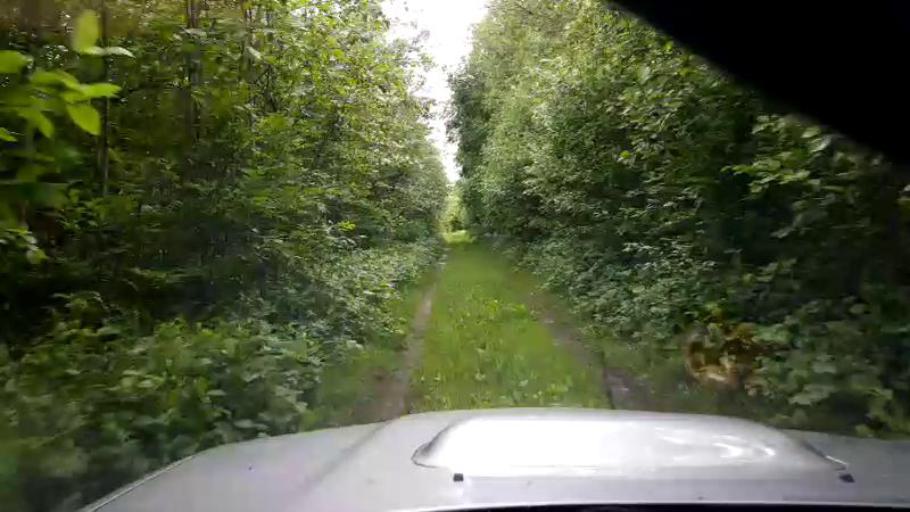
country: EE
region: Paernumaa
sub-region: Halinga vald
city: Parnu-Jaagupi
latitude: 58.5497
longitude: 24.5628
